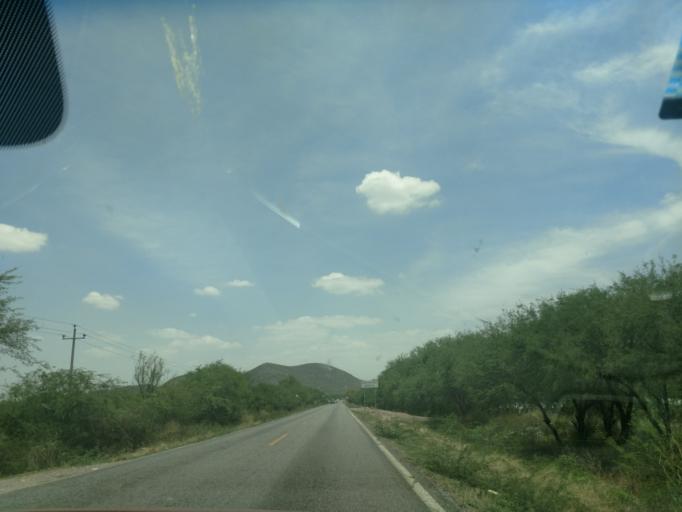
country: MX
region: San Luis Potosi
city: Ciudad Fernandez
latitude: 22.0084
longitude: -100.1527
